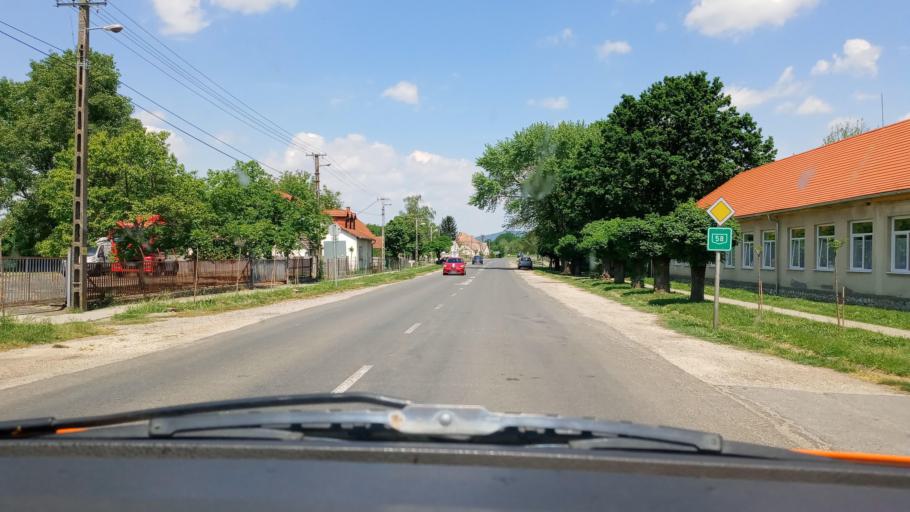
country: HU
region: Baranya
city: Harkany
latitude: 45.8065
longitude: 18.2113
